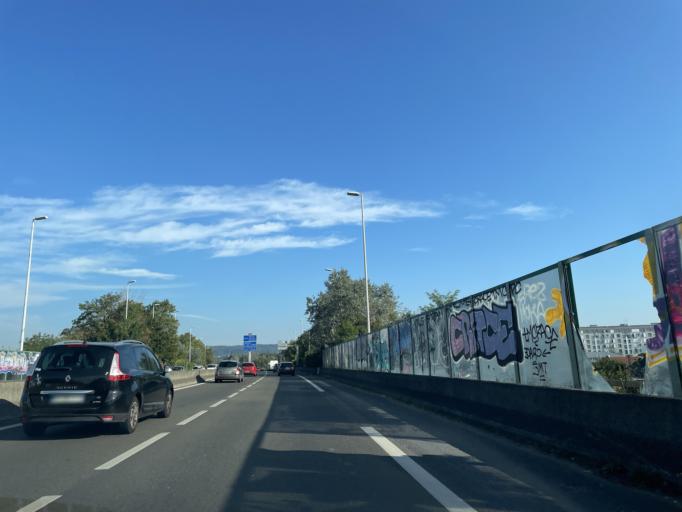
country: FR
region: Ile-de-France
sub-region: Departement du Val-d'Oise
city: Ermont
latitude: 48.9933
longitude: 2.2460
